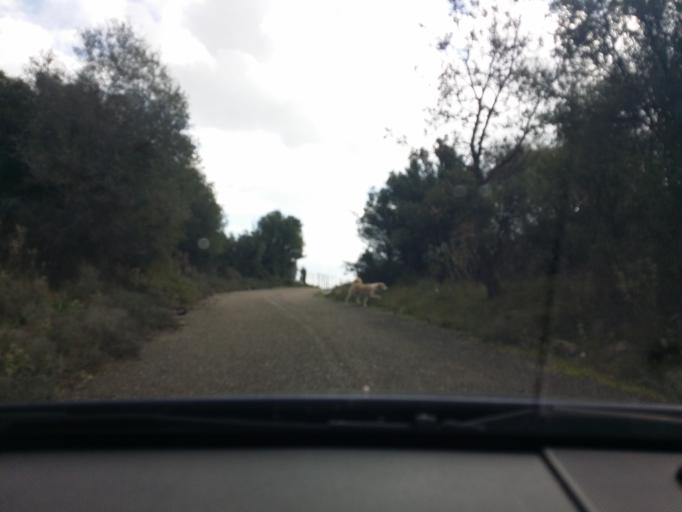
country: GR
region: West Greece
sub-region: Nomos Aitolias kai Akarnanias
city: Fitiai
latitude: 38.6751
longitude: 21.1900
